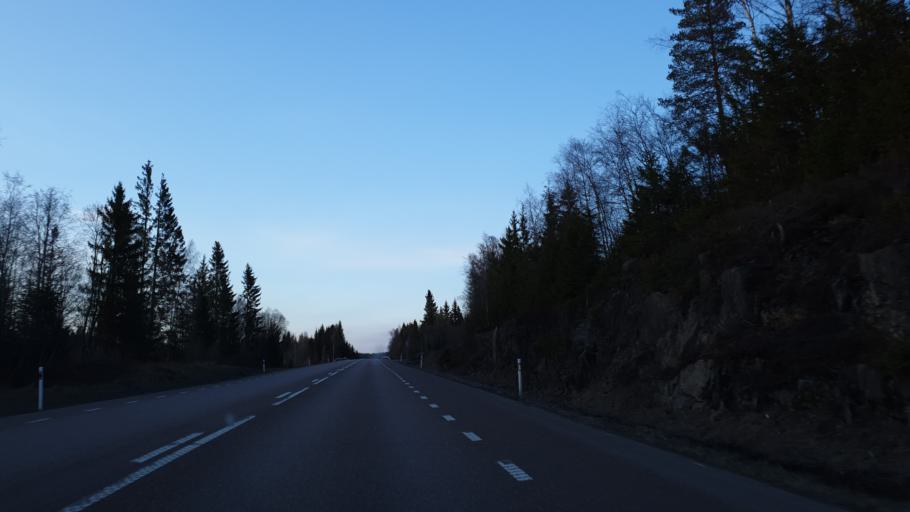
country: SE
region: Vaesternorrland
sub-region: Haernoesands Kommun
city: Haernoesand
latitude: 62.6966
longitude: 17.8536
